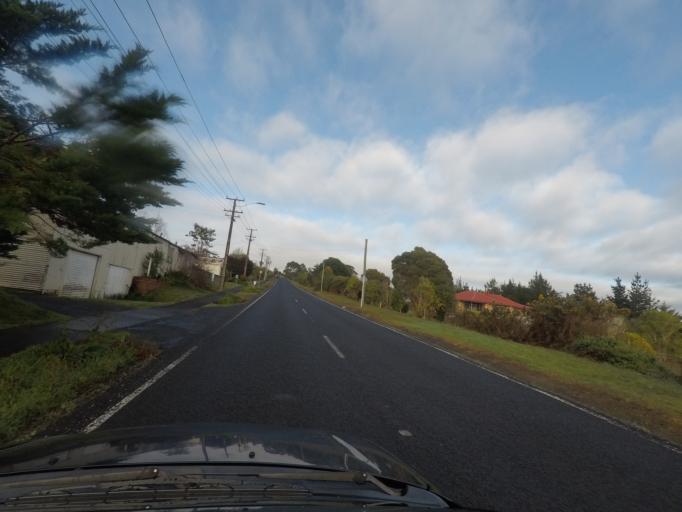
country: NZ
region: Auckland
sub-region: Auckland
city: Waitakere
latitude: -36.9009
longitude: 174.6143
